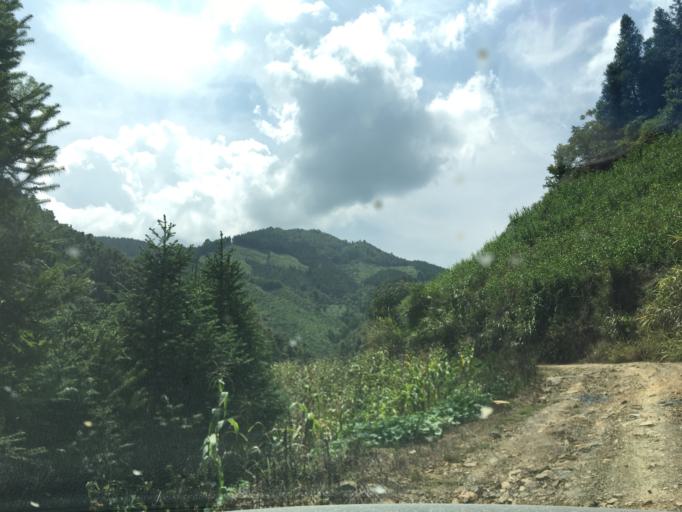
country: CN
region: Guangxi Zhuangzu Zizhiqu
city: Xinzhou
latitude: 24.9535
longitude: 105.7889
